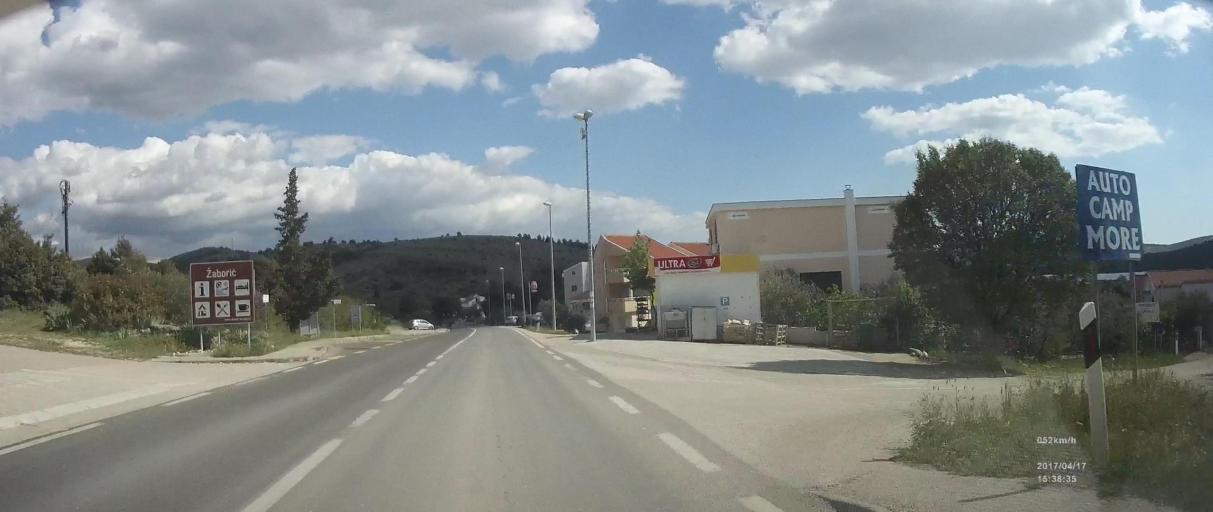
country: HR
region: Sibensko-Kniniska
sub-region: Grad Sibenik
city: Brodarica
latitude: 43.6633
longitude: 15.9446
